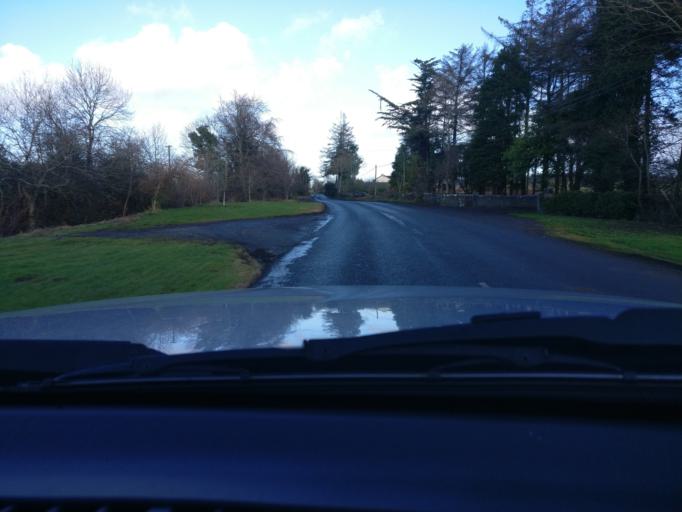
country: IE
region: Leinster
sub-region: An Iarmhi
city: Kilbeggan
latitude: 53.4343
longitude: -7.5528
